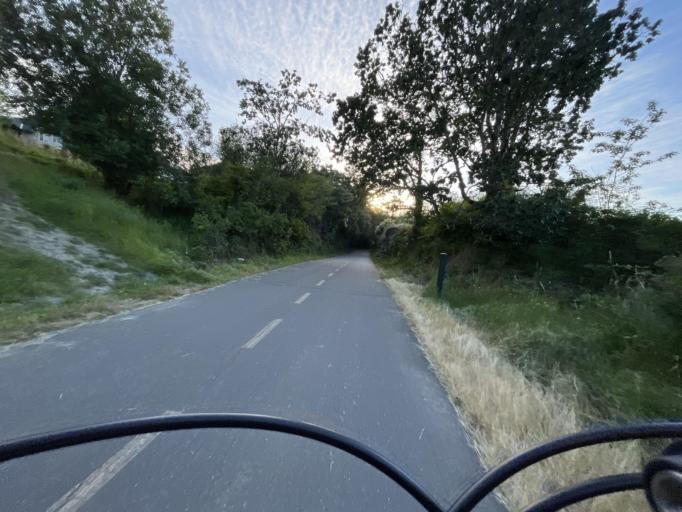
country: CA
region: British Columbia
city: Colwood
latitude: 48.4457
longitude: -123.4716
